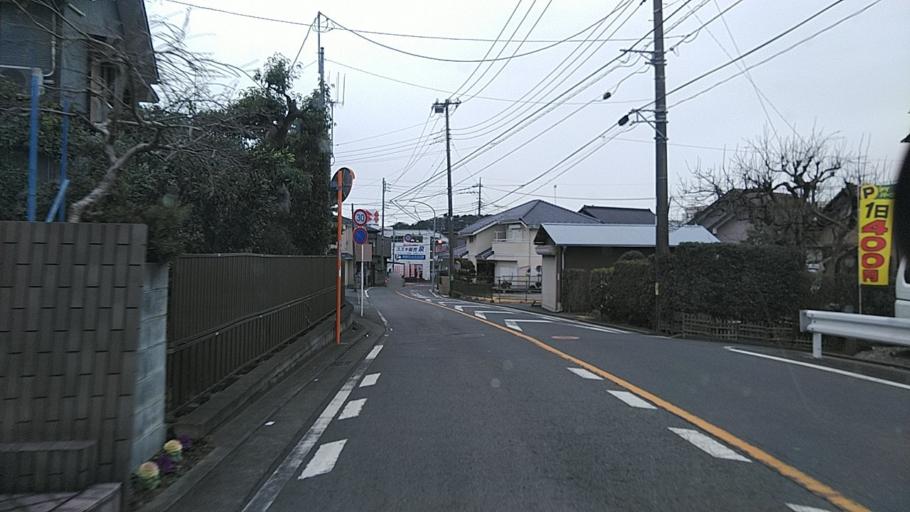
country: JP
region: Kanagawa
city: Fujisawa
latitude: 35.4004
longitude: 139.4879
